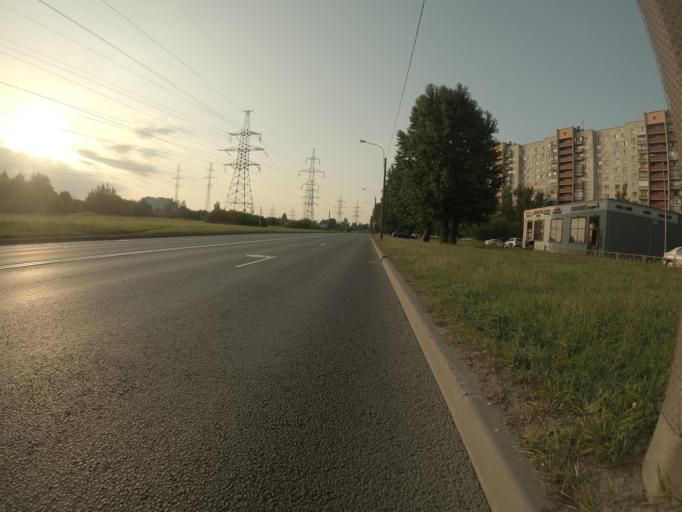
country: RU
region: St.-Petersburg
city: Krasnogvargeisky
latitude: 59.9506
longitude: 30.4609
